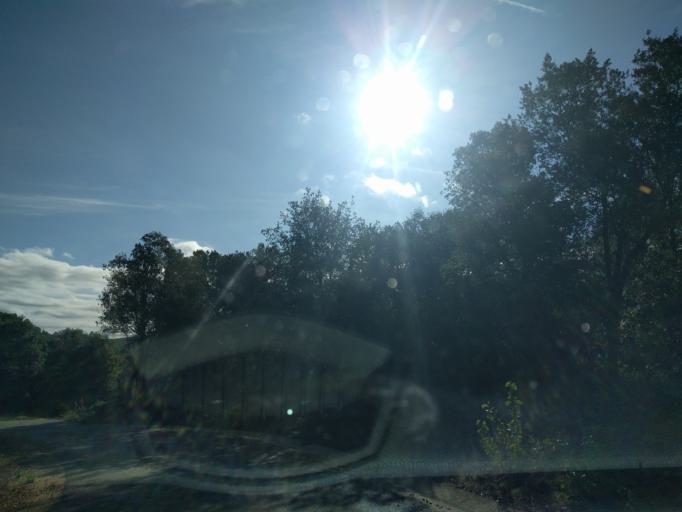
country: ES
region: Catalonia
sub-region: Provincia de Girona
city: la Cellera de Ter
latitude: 42.0223
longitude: 2.6277
